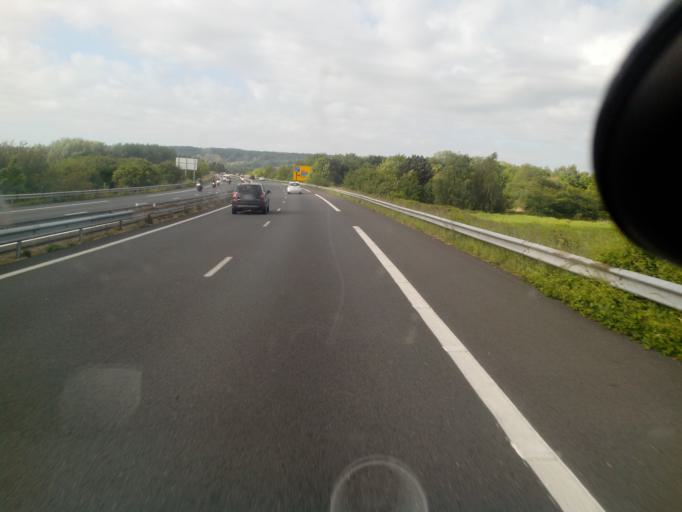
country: FR
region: Lower Normandy
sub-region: Departement du Calvados
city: Saint-Gatien-des-Bois
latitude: 49.2788
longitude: 0.1950
